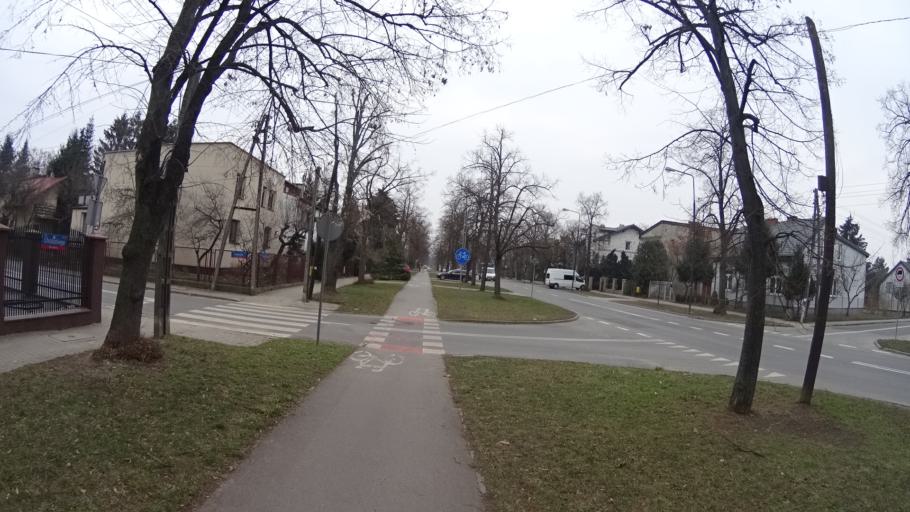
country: PL
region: Masovian Voivodeship
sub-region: Warszawa
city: Ursus
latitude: 52.2087
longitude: 20.8980
